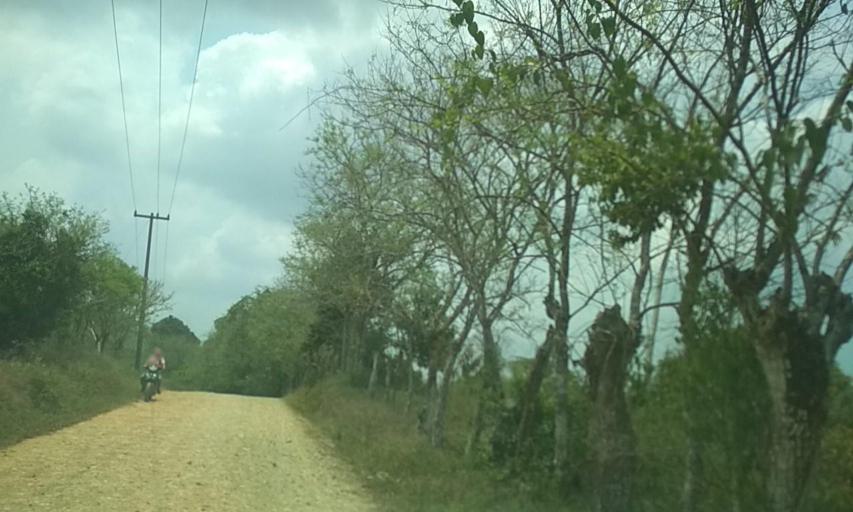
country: MX
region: Tabasco
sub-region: Huimanguillo
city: Francisco Rueda
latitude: 17.5787
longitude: -93.7894
